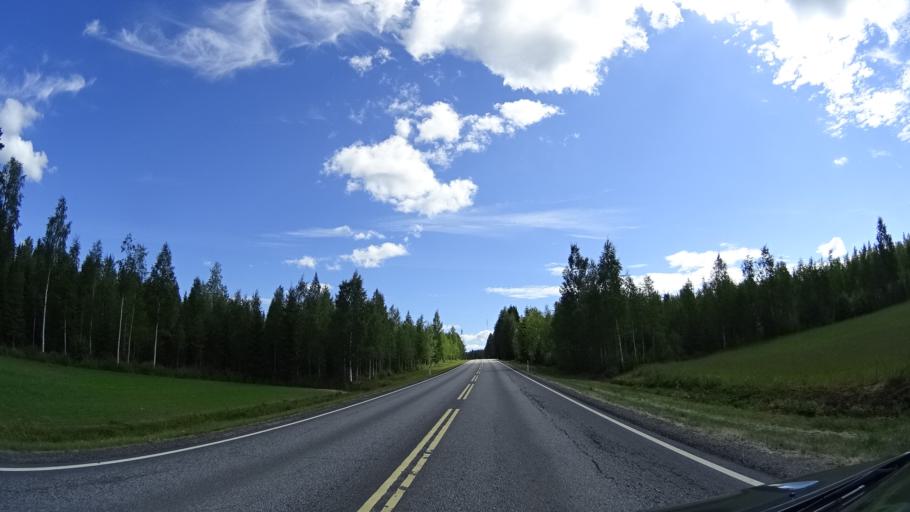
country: FI
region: Pirkanmaa
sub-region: Luoteis-Pirkanmaa
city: Kihnioe
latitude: 62.1997
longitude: 23.2005
